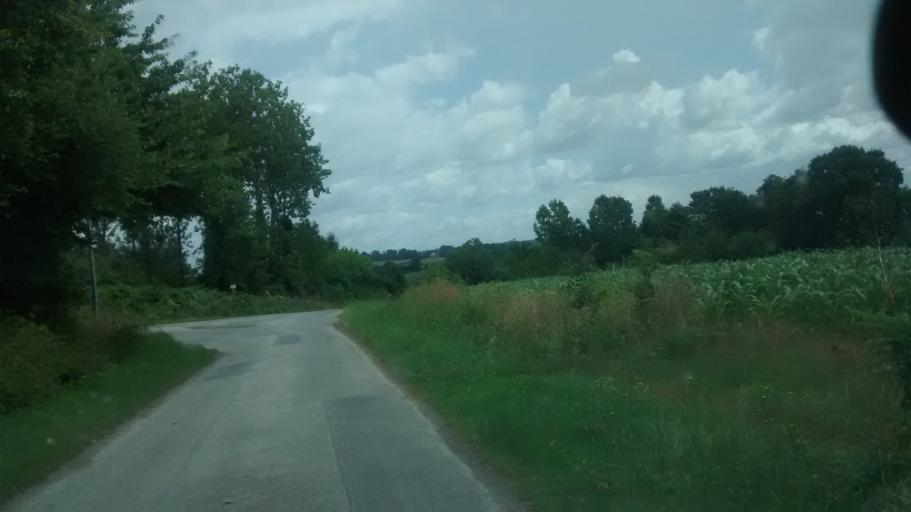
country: FR
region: Brittany
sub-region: Departement d'Ille-et-Vilaine
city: La Dominelais
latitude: 47.7771
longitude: -1.7370
